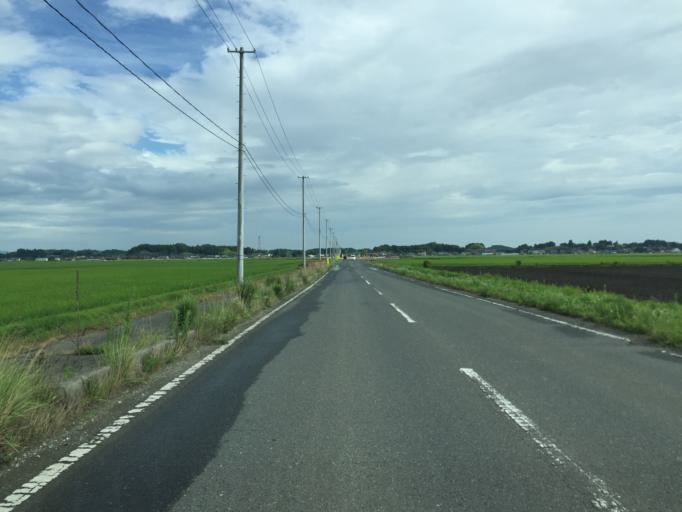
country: JP
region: Miyagi
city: Marumori
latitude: 37.7926
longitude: 140.9570
